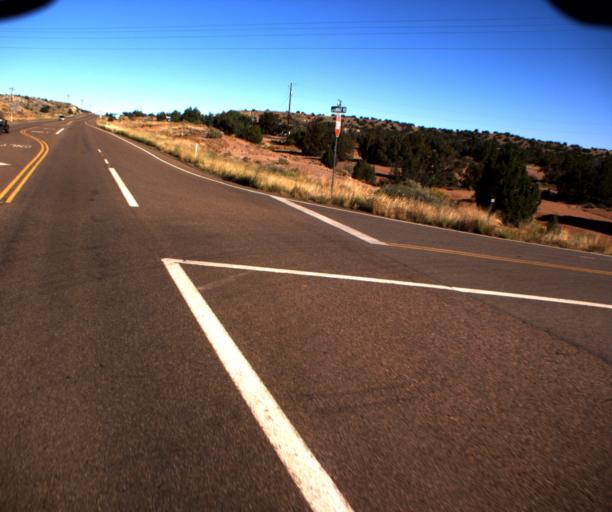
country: US
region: Arizona
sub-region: Navajo County
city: Taylor
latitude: 34.4062
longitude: -110.0768
